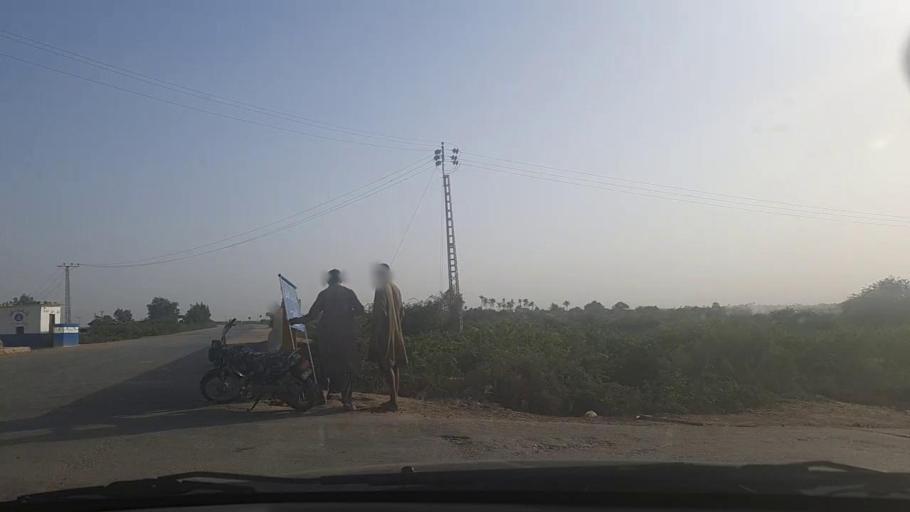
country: PK
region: Sindh
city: Keti Bandar
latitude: 24.2916
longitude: 67.6161
